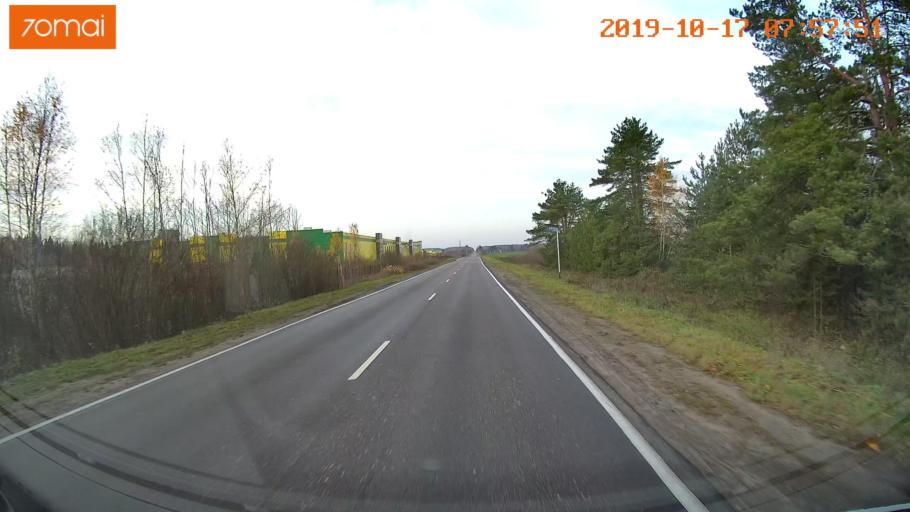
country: RU
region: Vladimir
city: Bavleny
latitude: 56.4082
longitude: 39.5688
